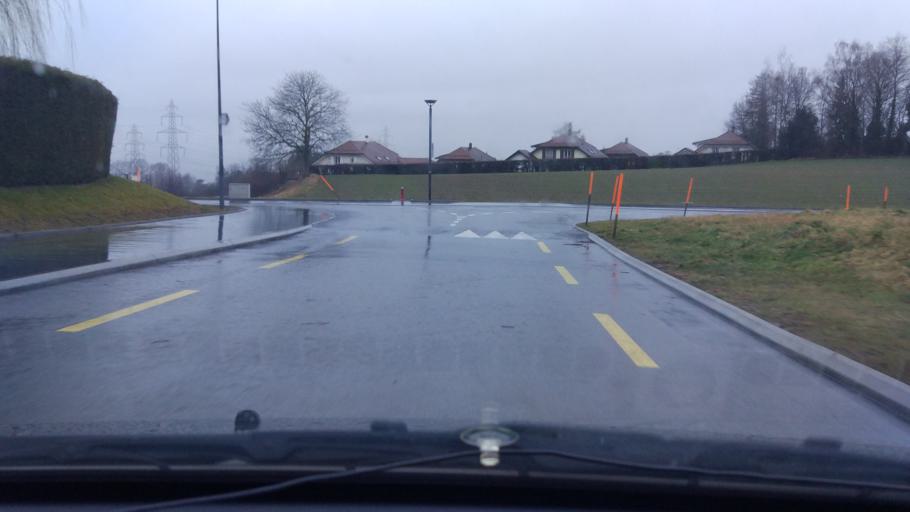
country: CH
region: Vaud
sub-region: Lausanne District
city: Romanel
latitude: 46.5603
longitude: 6.6100
